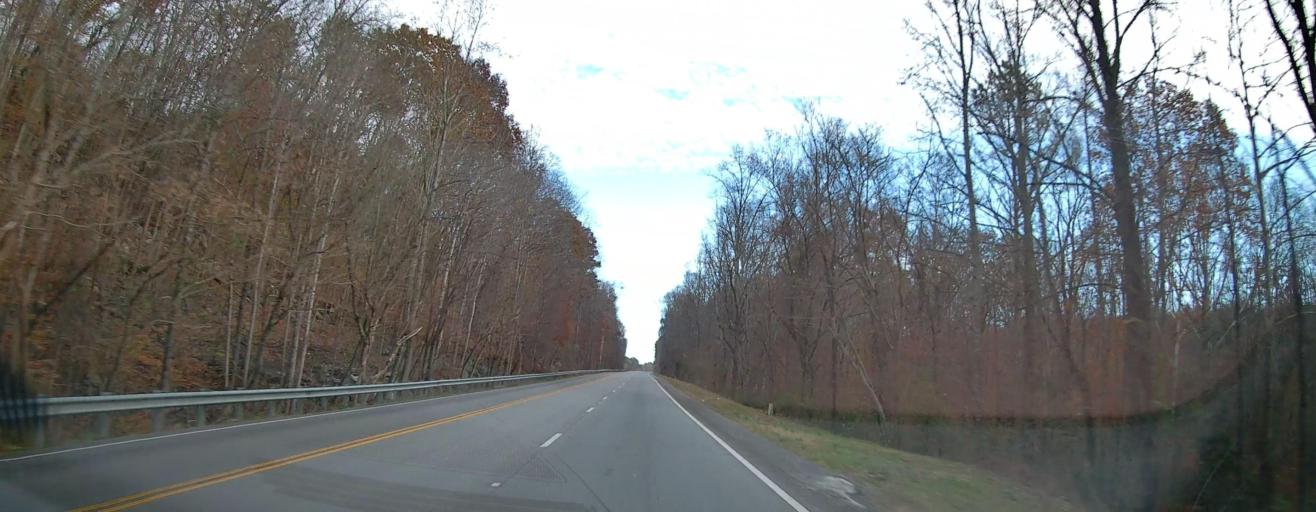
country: US
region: Alabama
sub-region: Marshall County
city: Arab
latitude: 34.3604
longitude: -86.6297
